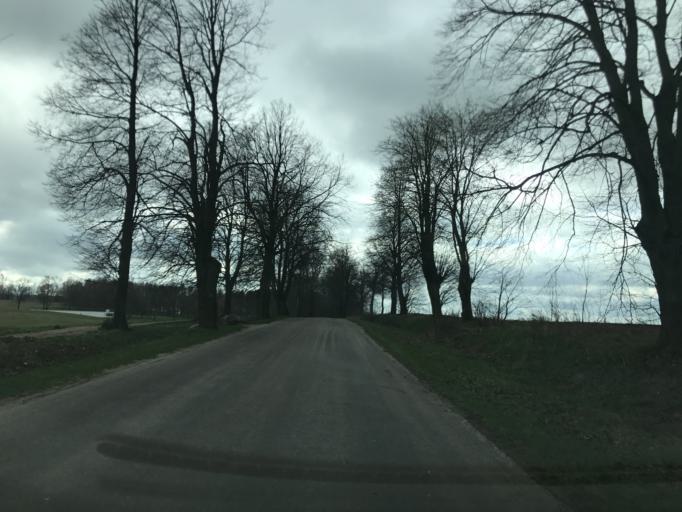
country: PL
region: Warmian-Masurian Voivodeship
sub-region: Powiat ostrodzki
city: Gierzwald
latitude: 53.4914
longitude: 20.1231
